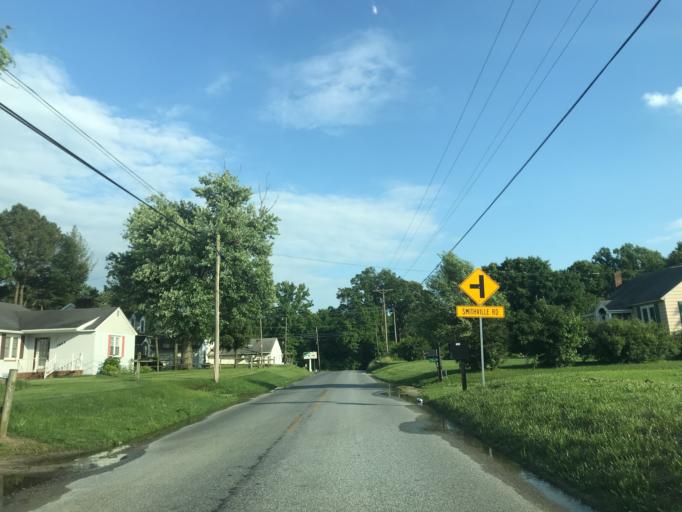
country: US
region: Maryland
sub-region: Caroline County
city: Federalsburg
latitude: 38.7135
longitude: -75.7778
